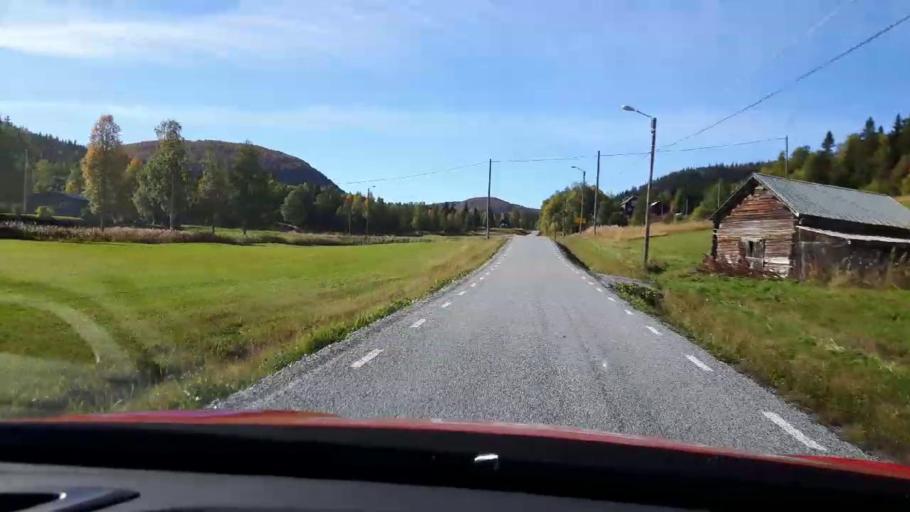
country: NO
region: Nord-Trondelag
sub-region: Royrvik
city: Royrvik
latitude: 64.7286
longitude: 13.9540
